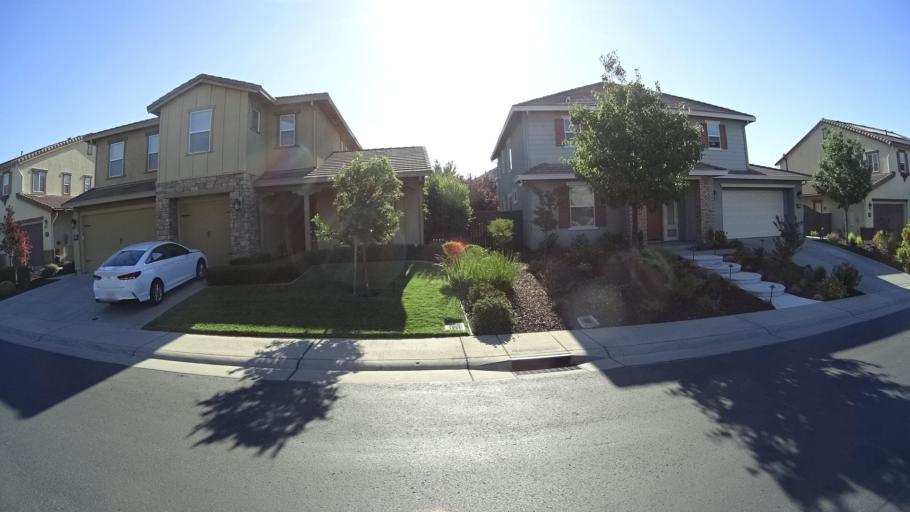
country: US
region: California
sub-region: Placer County
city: Rocklin
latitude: 38.8263
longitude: -121.2789
